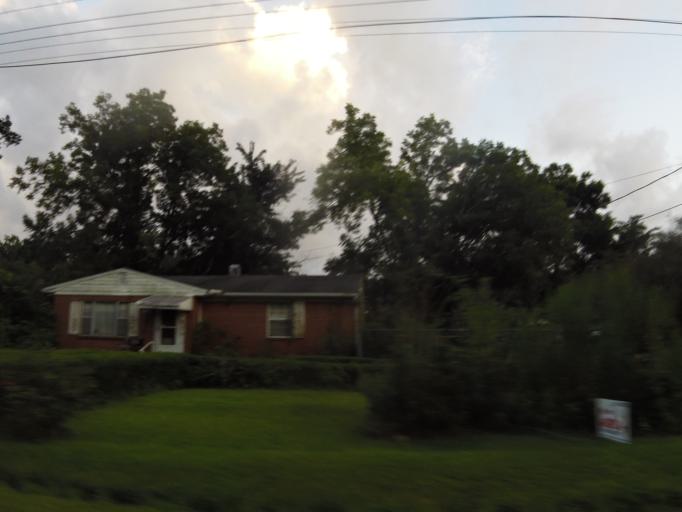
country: US
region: Florida
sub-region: Duval County
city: Jacksonville
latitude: 30.3309
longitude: -81.7249
